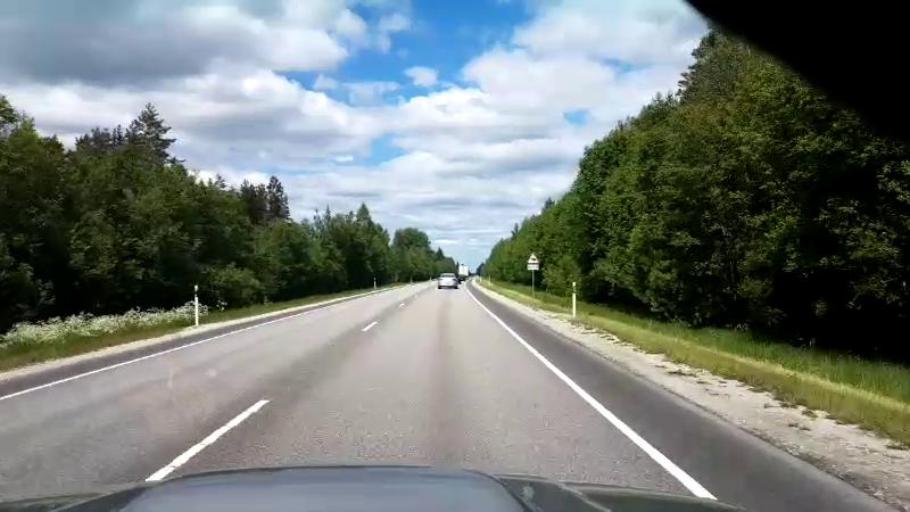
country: EE
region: Paernumaa
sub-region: Halinga vald
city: Parnu-Jaagupi
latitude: 58.7118
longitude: 24.4239
